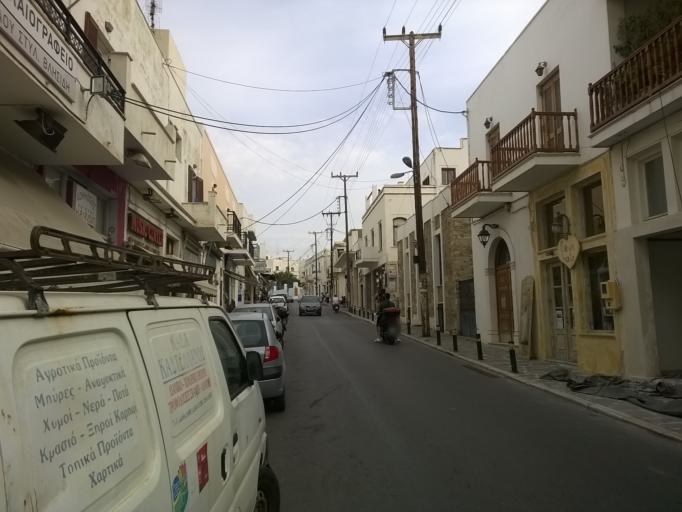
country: GR
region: South Aegean
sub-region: Nomos Kykladon
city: Naxos
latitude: 37.1034
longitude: 25.3761
